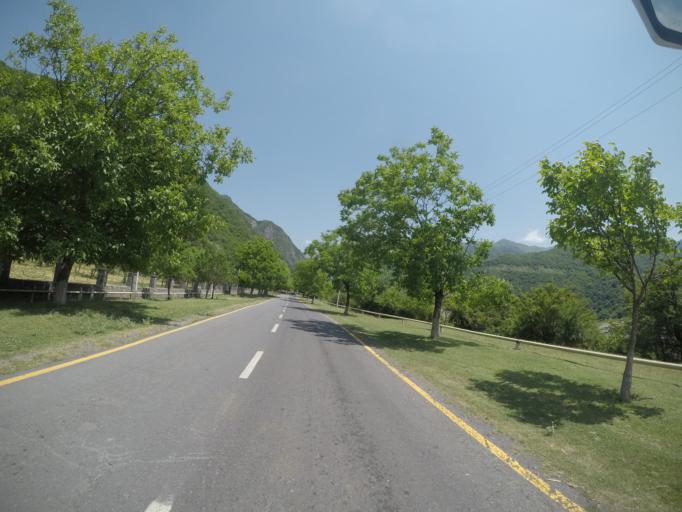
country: AZ
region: Qakh Rayon
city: Qaxbas
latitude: 41.4482
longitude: 46.9998
